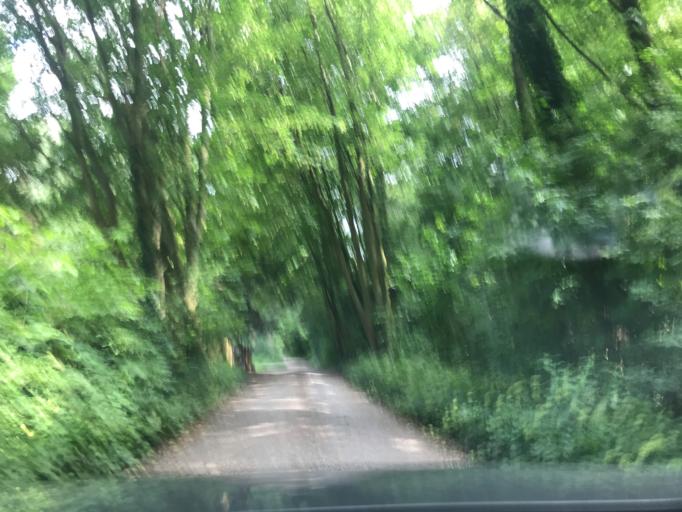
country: DE
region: North Rhine-Westphalia
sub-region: Regierungsbezirk Dusseldorf
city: Neuss
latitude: 51.1281
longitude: 6.7404
